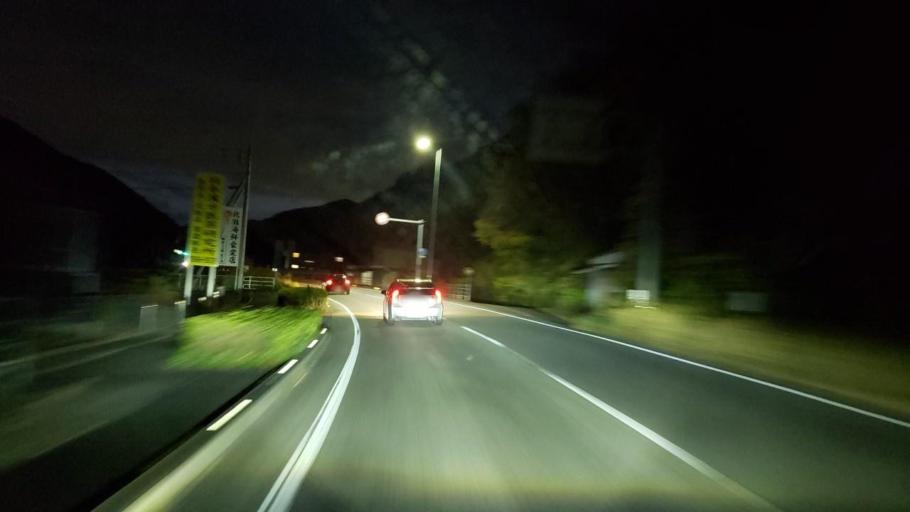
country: JP
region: Tokushima
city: Narutocho-mitsuishi
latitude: 34.2157
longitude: 134.5590
